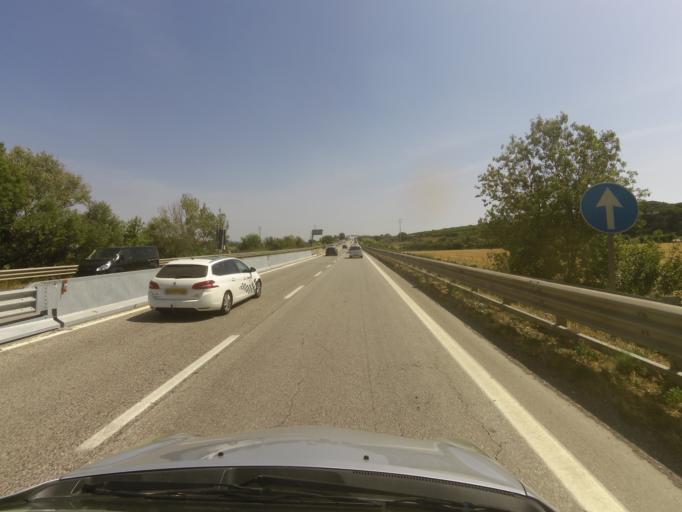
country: IT
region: Tuscany
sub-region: Provincia di Livorno
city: Cecina
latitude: 43.3225
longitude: 10.5313
